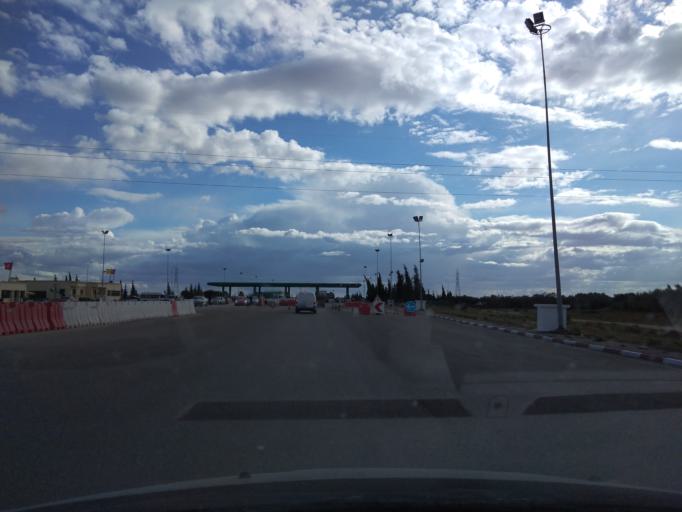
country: TN
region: Susah
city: Masakin
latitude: 35.6920
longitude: 10.5636
